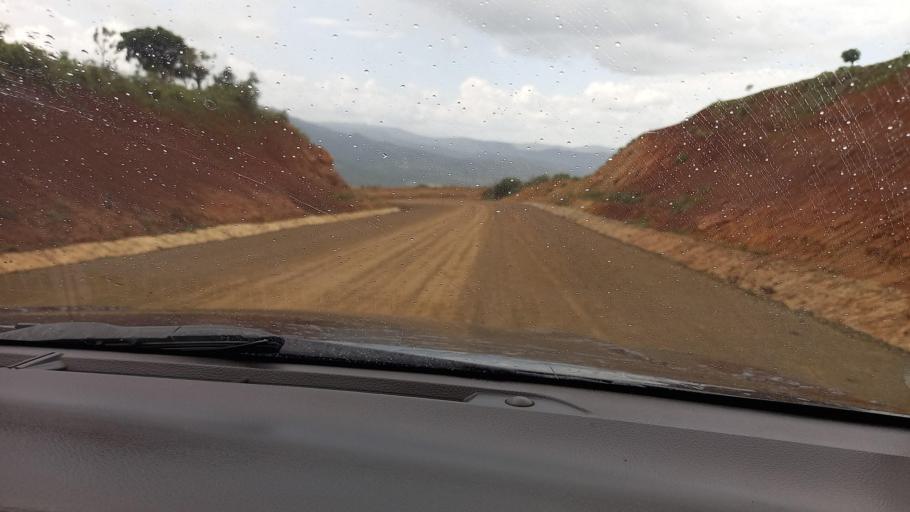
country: ET
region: Southern Nations, Nationalities, and People's Region
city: Mizan Teferi
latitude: 6.1809
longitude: 35.7003
